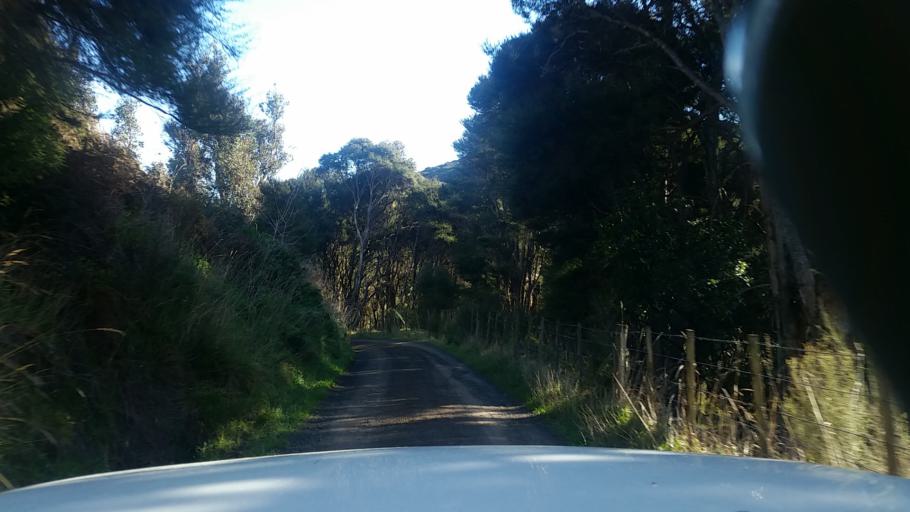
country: NZ
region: Canterbury
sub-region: Christchurch City
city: Christchurch
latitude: -43.7927
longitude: 172.9966
